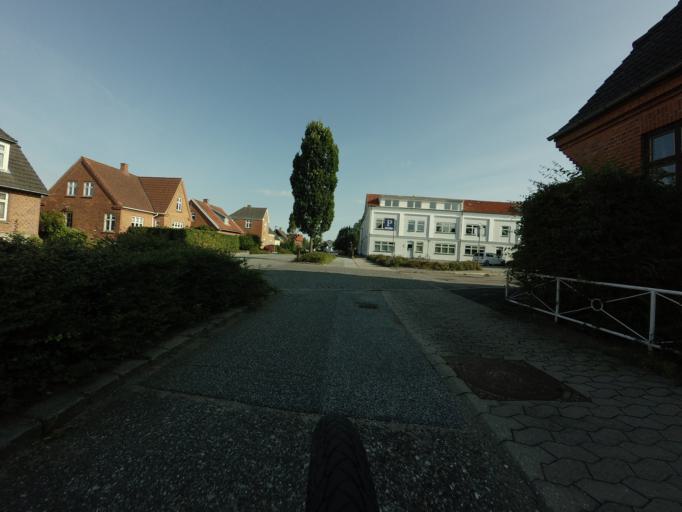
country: DK
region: Zealand
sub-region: Soro Kommune
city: Soro
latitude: 55.4410
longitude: 11.5600
